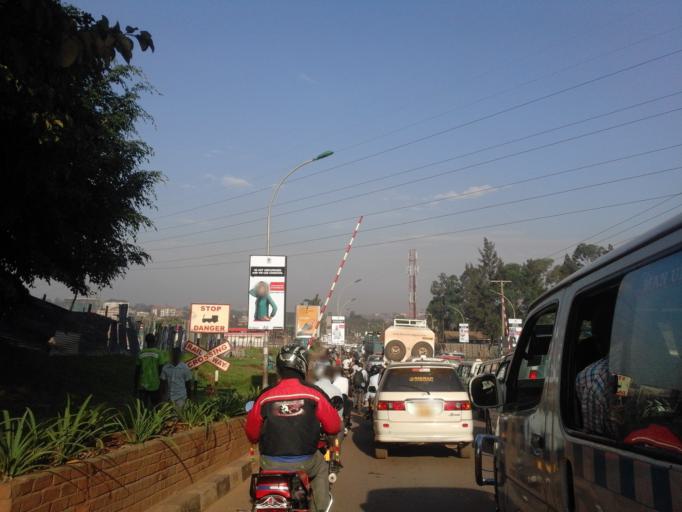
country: UG
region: Central Region
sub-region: Kampala District
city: Kampala
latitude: 0.3071
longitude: 32.5821
